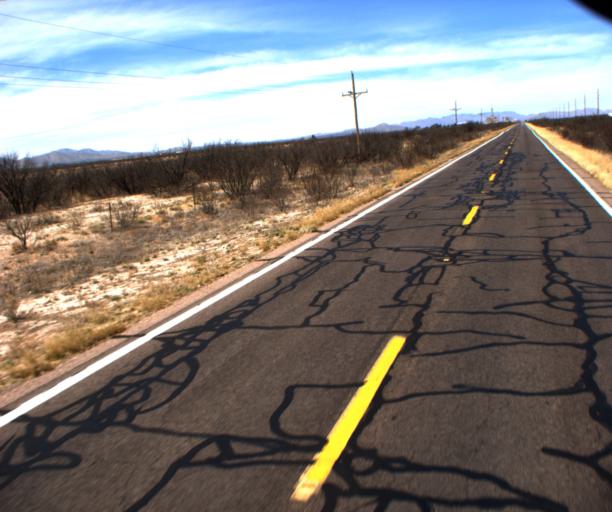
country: US
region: Arizona
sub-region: Cochise County
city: Willcox
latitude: 32.0203
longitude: -109.8711
